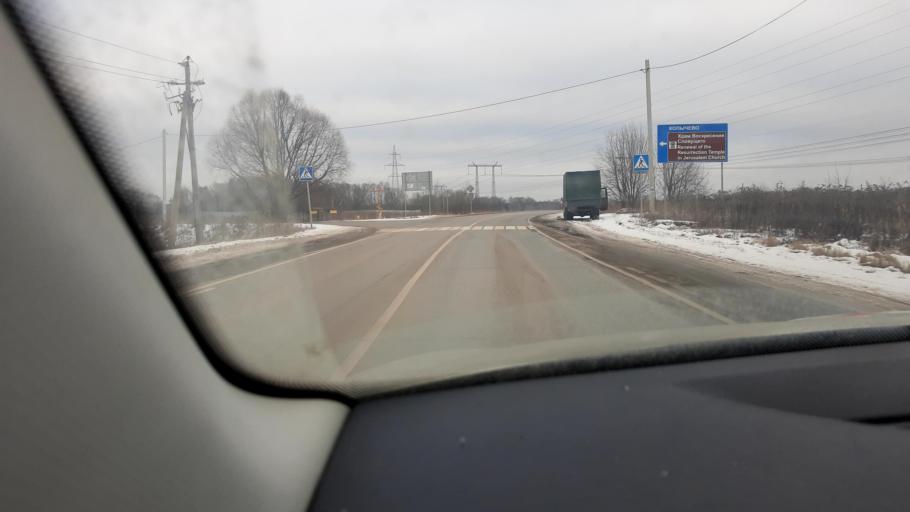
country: RU
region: Moskovskaya
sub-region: Leninskiy Rayon
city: Molokovo
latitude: 55.4866
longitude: 37.8598
